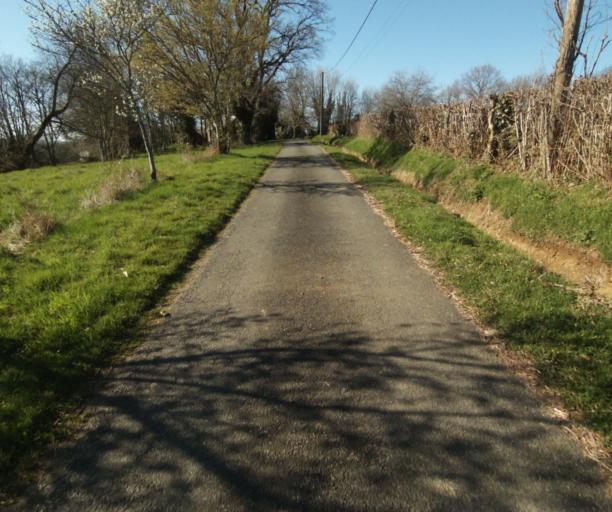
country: FR
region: Limousin
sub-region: Departement de la Correze
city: Chamboulive
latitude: 45.4049
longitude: 1.6610
